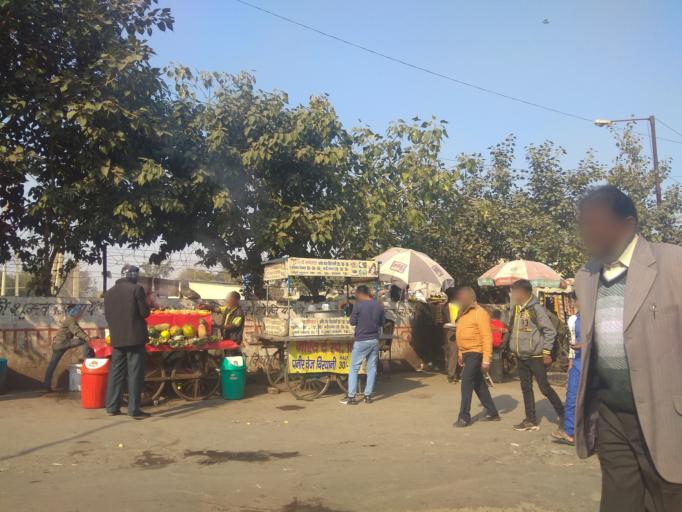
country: IN
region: NCT
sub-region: West Delhi
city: Nangloi Jat
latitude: 28.6254
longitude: 77.0663
